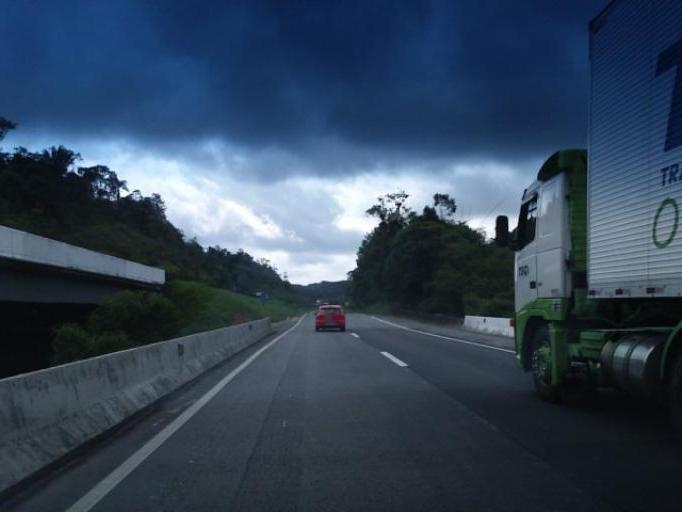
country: BR
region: Parana
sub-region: Antonina
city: Antonina
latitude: -25.0983
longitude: -48.6822
